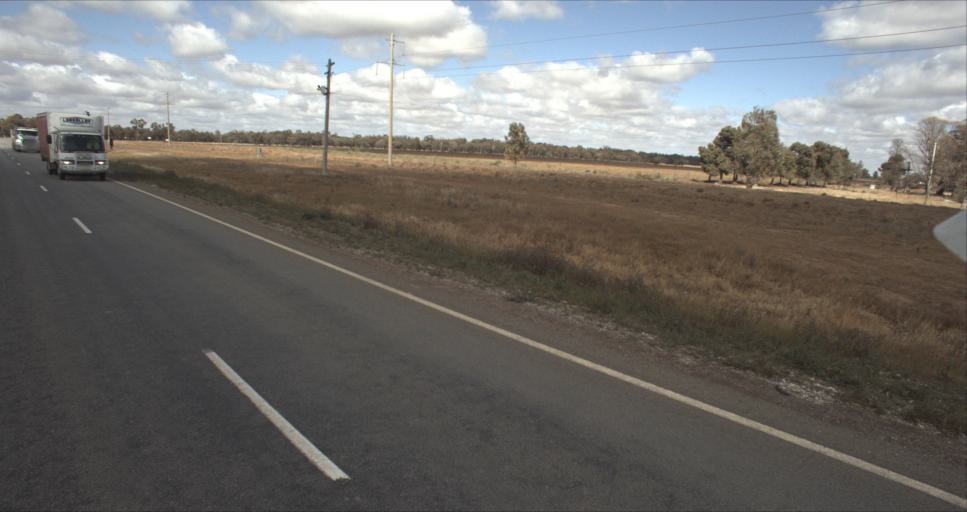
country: AU
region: New South Wales
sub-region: Murrumbidgee Shire
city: Darlington Point
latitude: -34.5927
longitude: 146.1633
